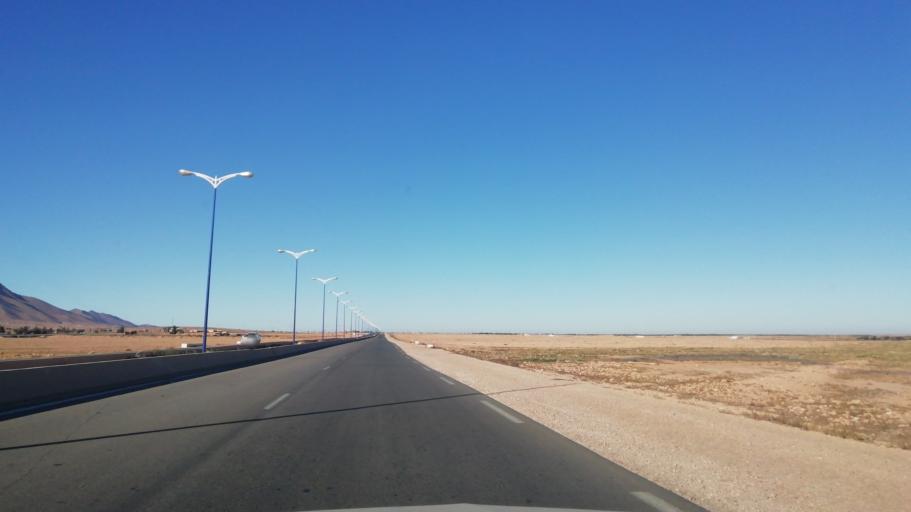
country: DZ
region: Wilaya de Naama
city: Naama
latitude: 33.5698
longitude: -0.2407
